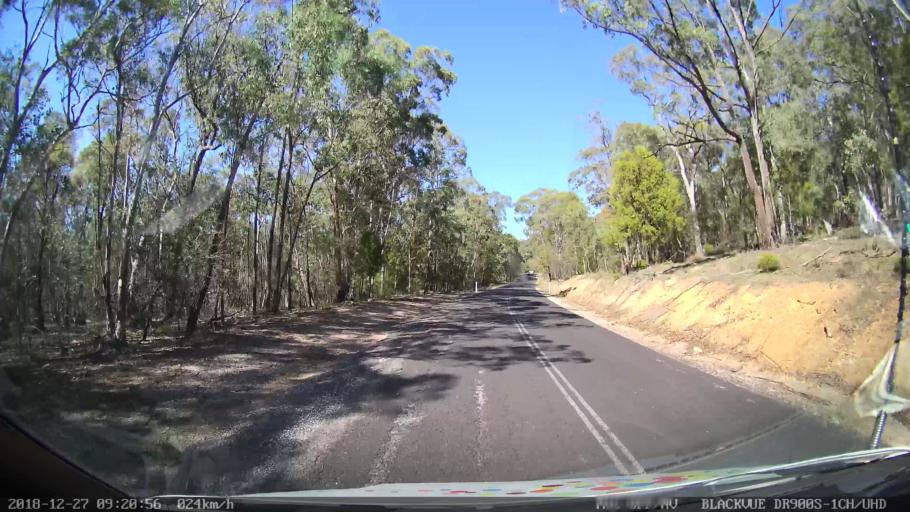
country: AU
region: New South Wales
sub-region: Lithgow
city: Portland
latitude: -33.1213
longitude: 150.0205
